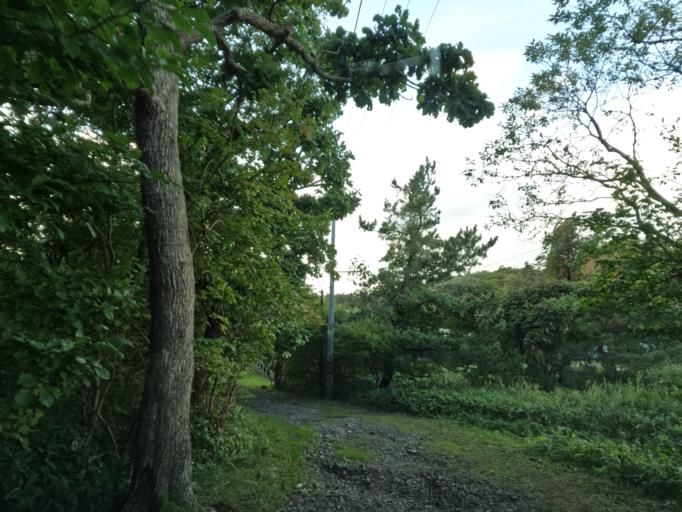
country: JP
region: Hokkaido
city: Muroran
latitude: 42.3758
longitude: 140.9136
